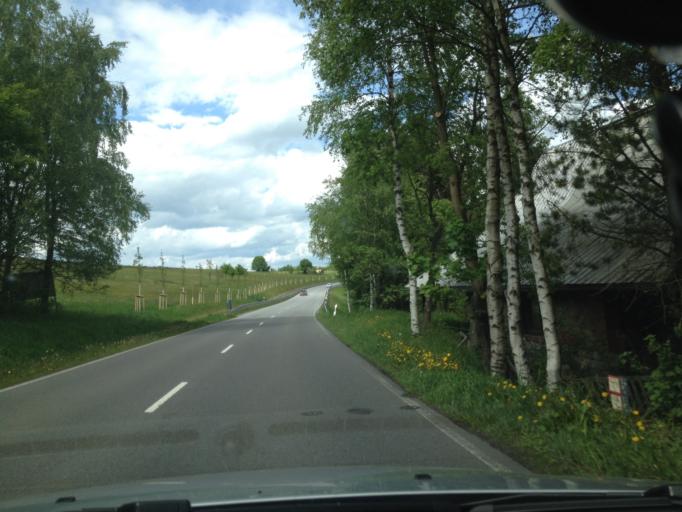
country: DE
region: Saxony
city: Barenstein
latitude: 50.5097
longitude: 13.0267
